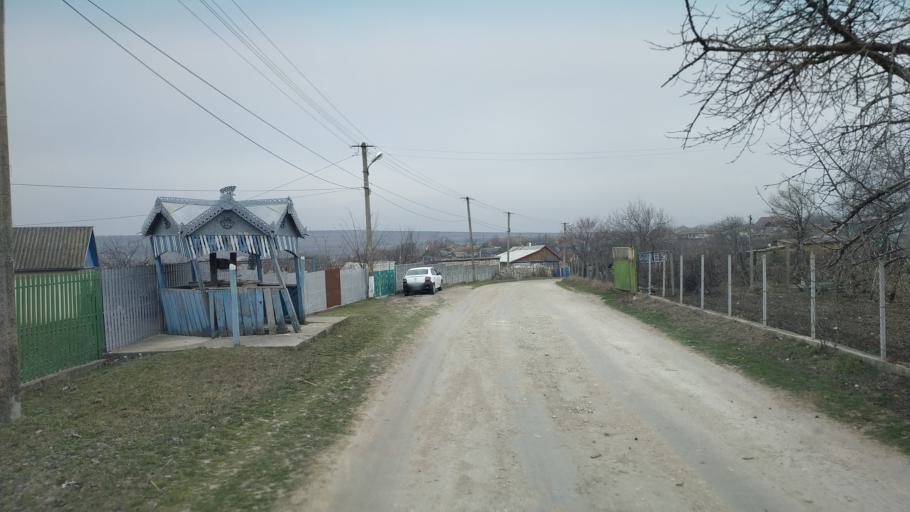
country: MD
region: Chisinau
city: Singera
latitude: 46.8246
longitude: 29.0280
